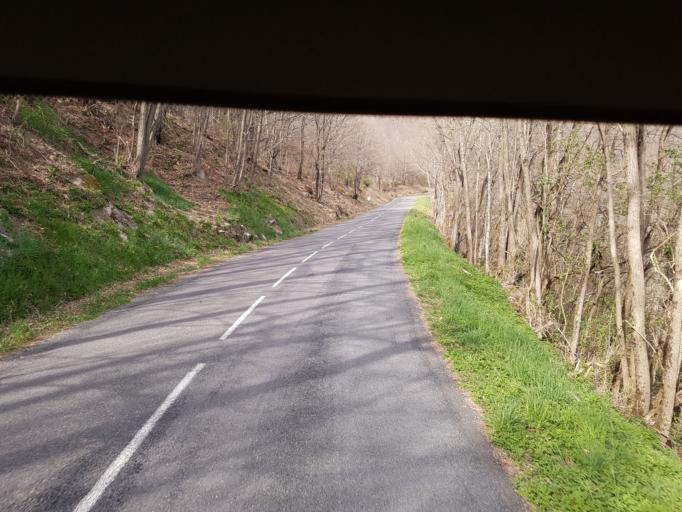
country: FR
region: Languedoc-Roussillon
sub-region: Departement de la Lozere
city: Florac
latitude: 44.3612
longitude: 3.6700
